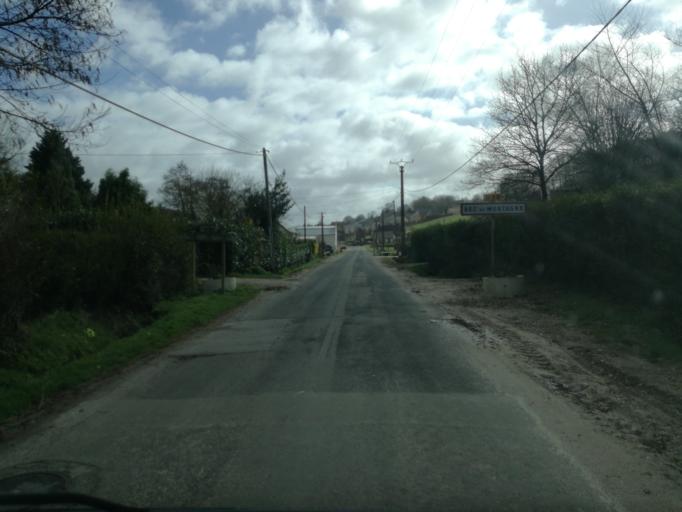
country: FR
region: Haute-Normandie
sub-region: Departement de la Seine-Maritime
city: Bretteville-du-Grand-Caux
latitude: 49.7054
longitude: 0.4406
